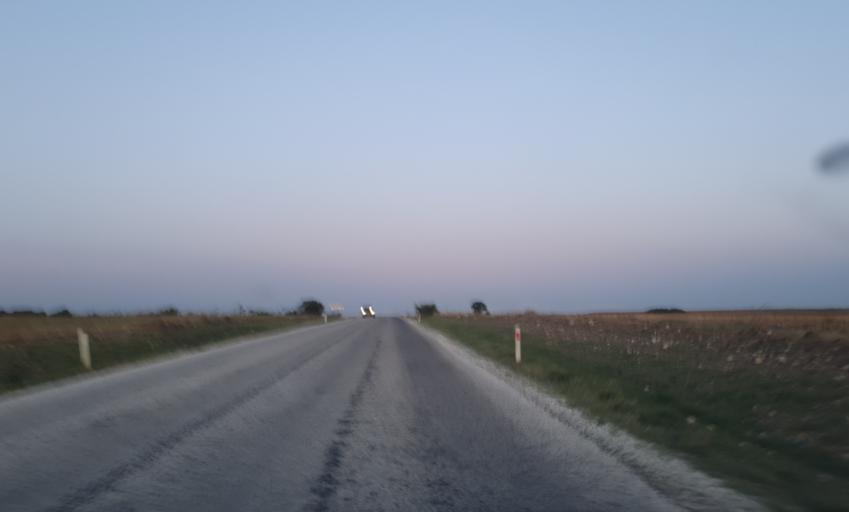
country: TR
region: Kirklareli
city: Pinarhisar
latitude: 41.6272
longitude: 27.5735
